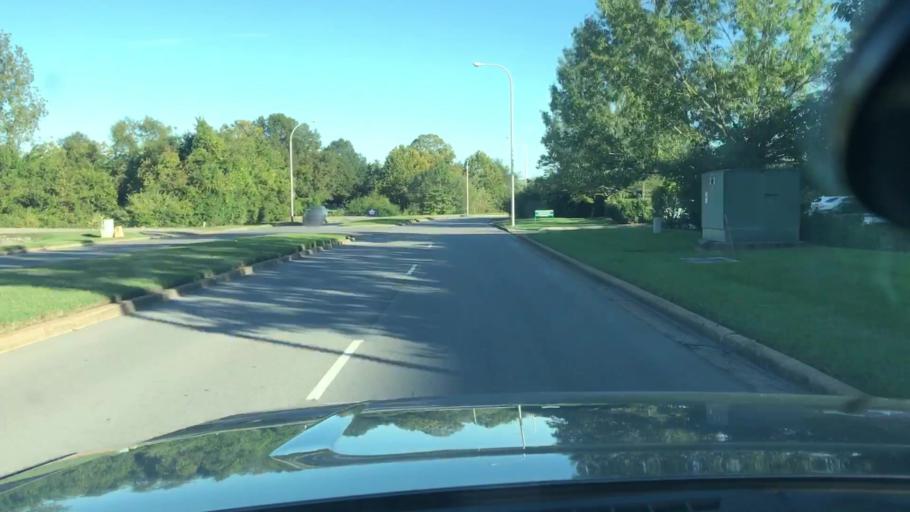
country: US
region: Tennessee
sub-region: Davidson County
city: Nashville
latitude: 36.1982
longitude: -86.7947
